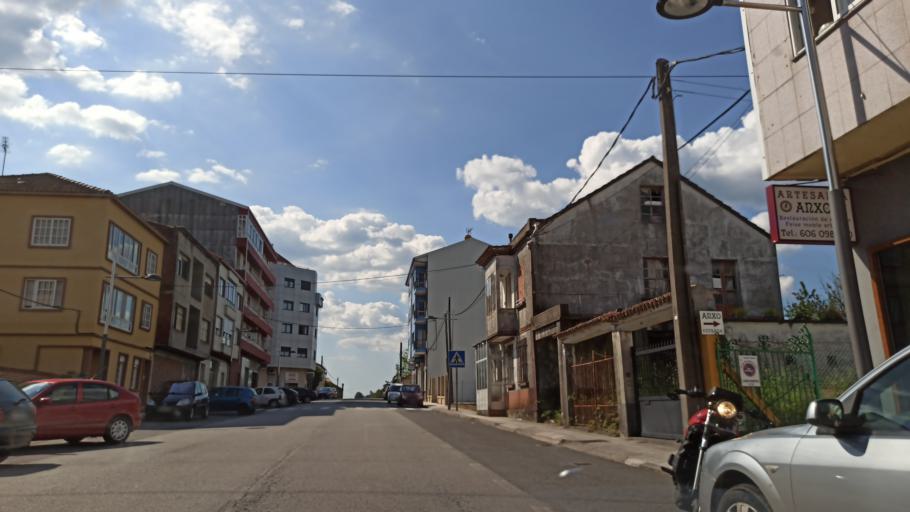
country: ES
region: Galicia
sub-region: Provincia da Coruna
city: Negreira
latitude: 42.9128
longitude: -8.7386
